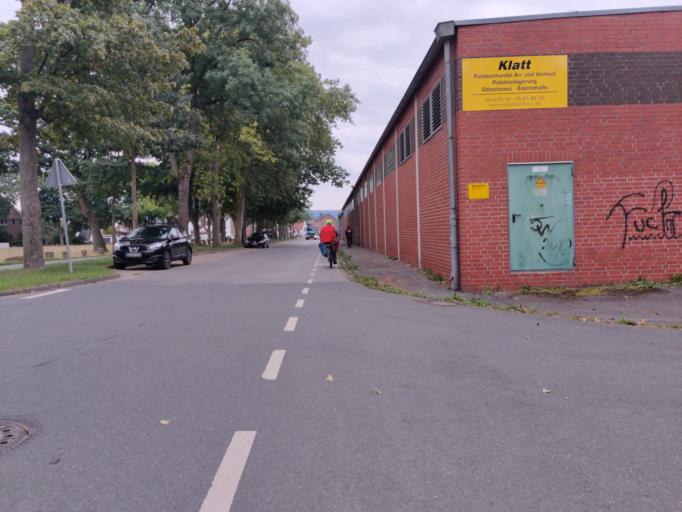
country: DE
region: Lower Saxony
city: Holzminden
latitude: 51.8335
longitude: 9.4418
